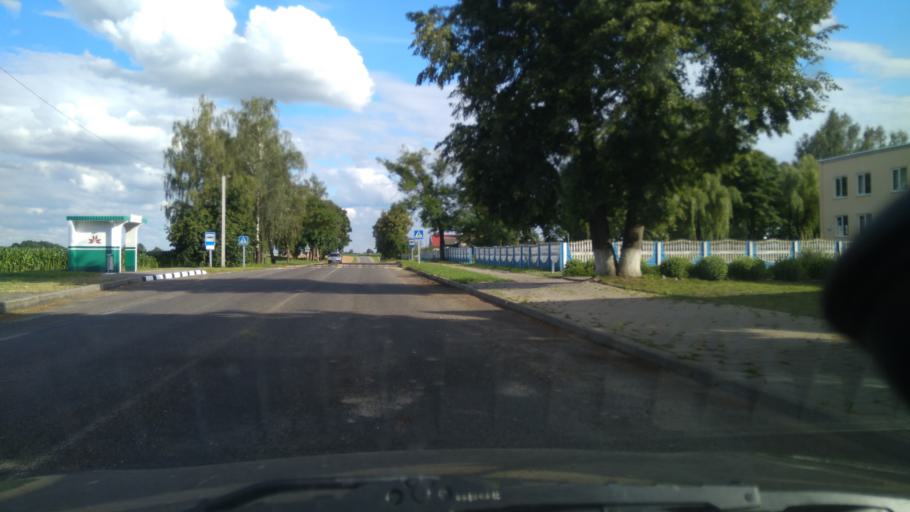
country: BY
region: Grodnenskaya
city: Masty
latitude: 53.3207
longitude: 24.6862
